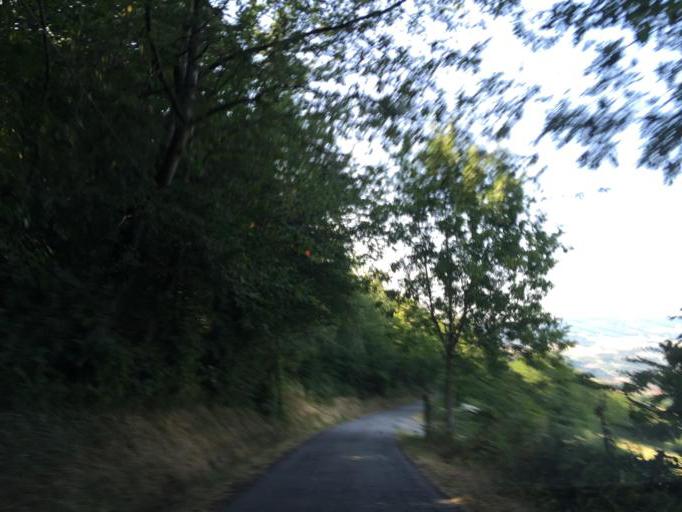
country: FR
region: Rhone-Alpes
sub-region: Departement de la Loire
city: Saint-Chamond
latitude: 45.4428
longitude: 4.5013
